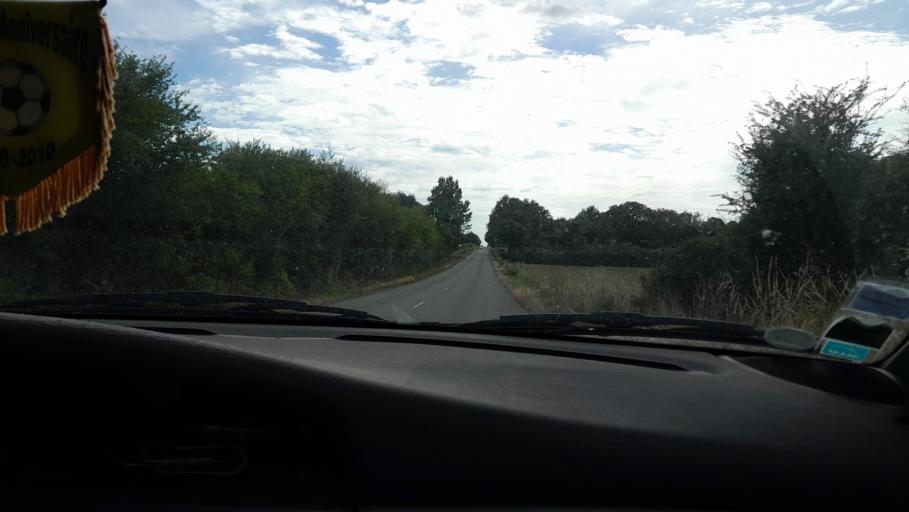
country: FR
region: Brittany
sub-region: Departement d'Ille-et-Vilaine
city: Le Pertre
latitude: 47.9792
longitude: -1.0151
